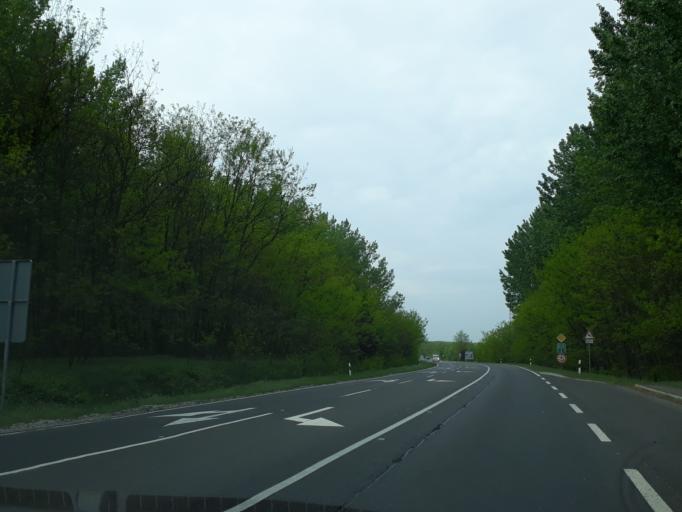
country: HU
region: Szabolcs-Szatmar-Bereg
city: Nyirbogdany
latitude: 48.0502
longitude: 21.8946
